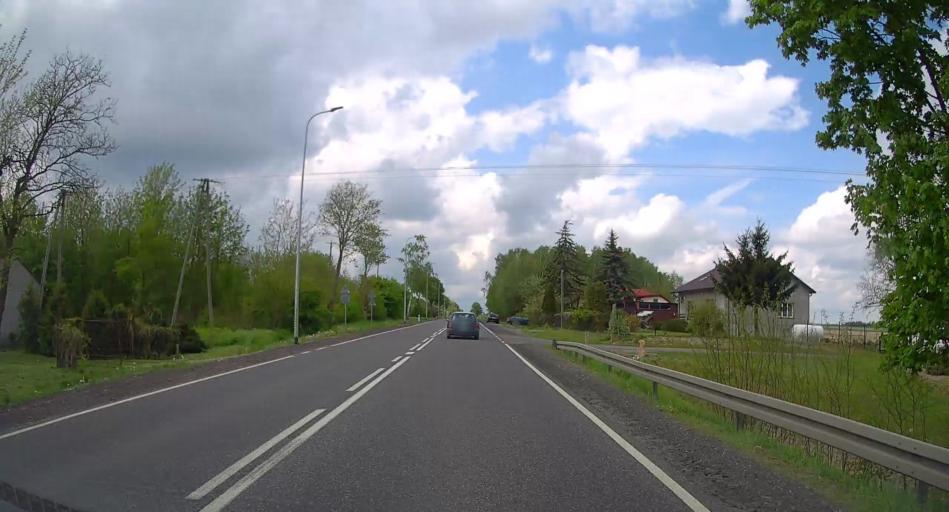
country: PL
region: Masovian Voivodeship
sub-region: Powiat nowodworski
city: Zakroczym
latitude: 52.4422
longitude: 20.5422
